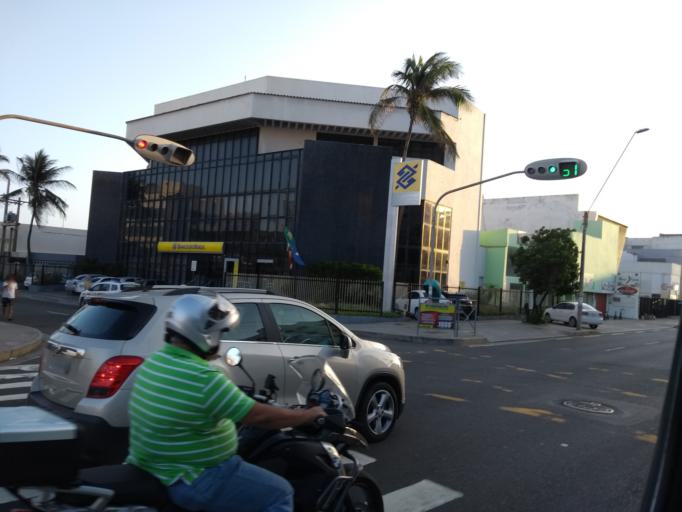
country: BR
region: Bahia
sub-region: Salvador
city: Salvador
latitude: -13.0094
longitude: -38.4654
